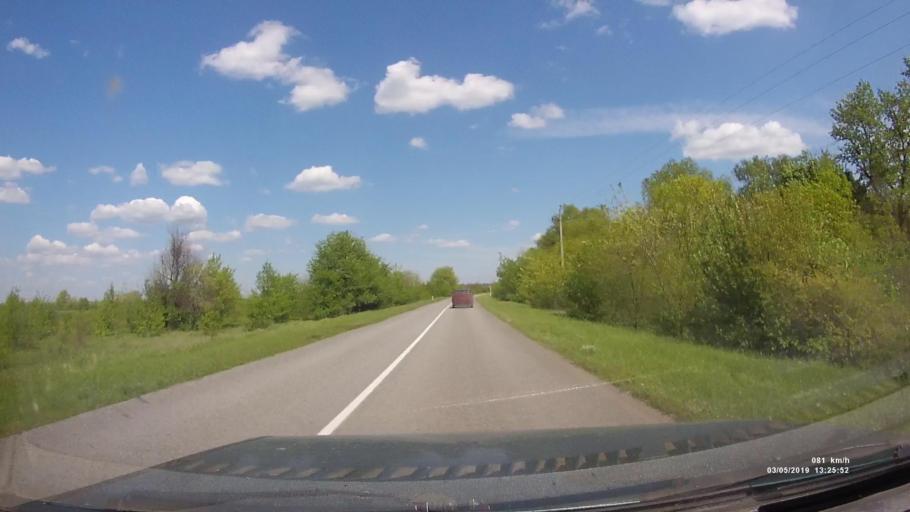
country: RU
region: Rostov
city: Semikarakorsk
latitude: 47.5695
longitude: 40.8098
